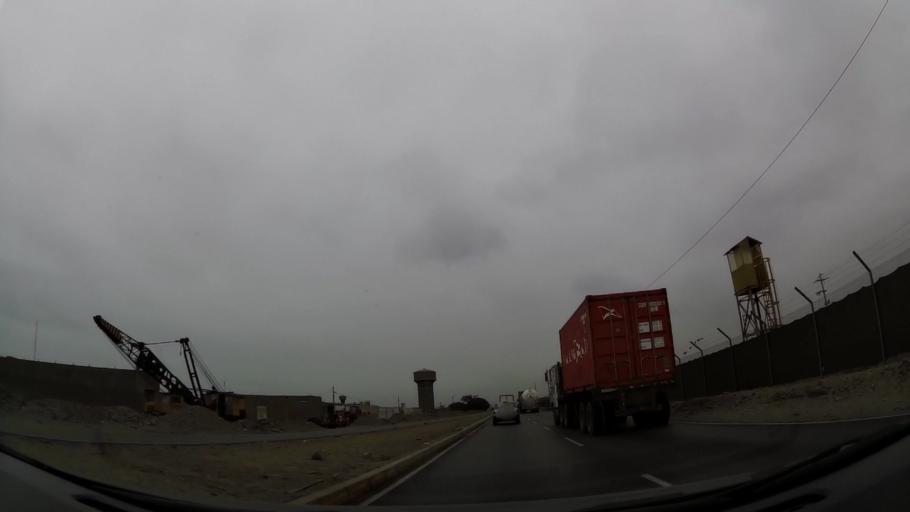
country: PE
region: Callao
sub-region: Callao
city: Callao
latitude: -12.0079
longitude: -77.1278
